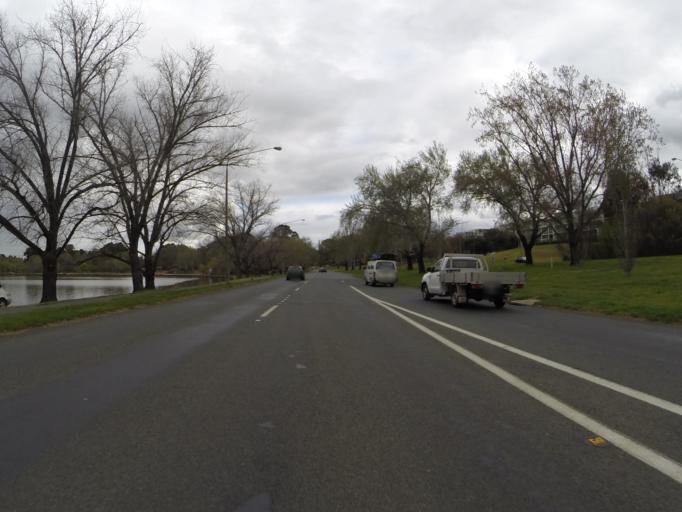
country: AU
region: Australian Capital Territory
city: Forrest
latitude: -35.3058
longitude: 149.1400
